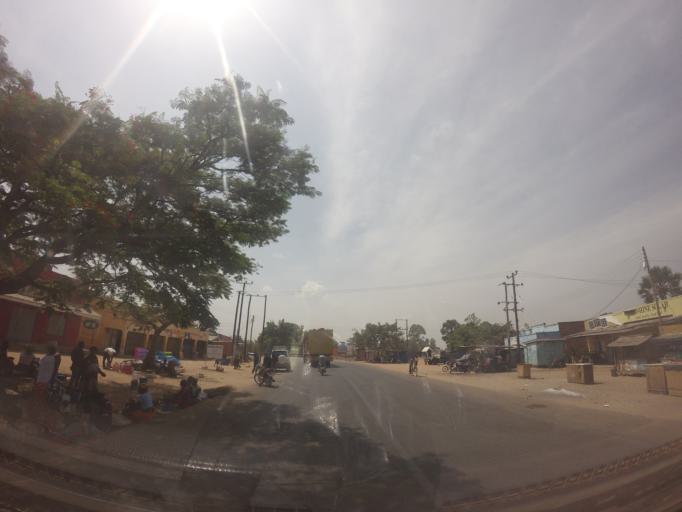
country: UG
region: Northern Region
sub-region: Arua District
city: Arua
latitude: 2.9570
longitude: 30.9165
